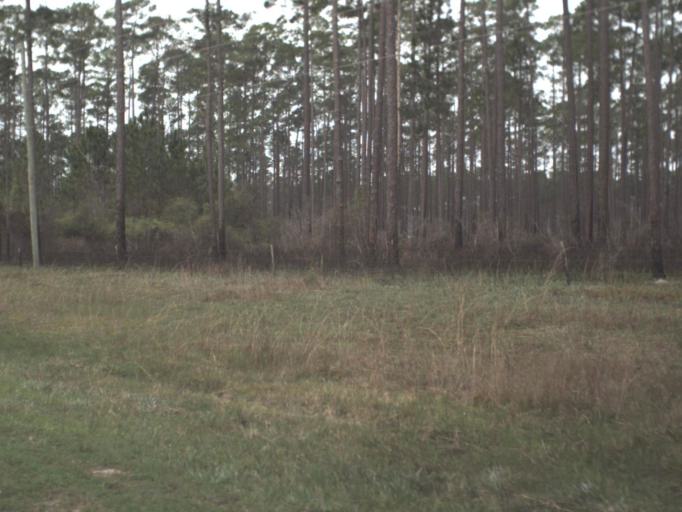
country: US
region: Florida
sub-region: Gulf County
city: Wewahitchka
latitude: 30.1696
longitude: -84.9500
